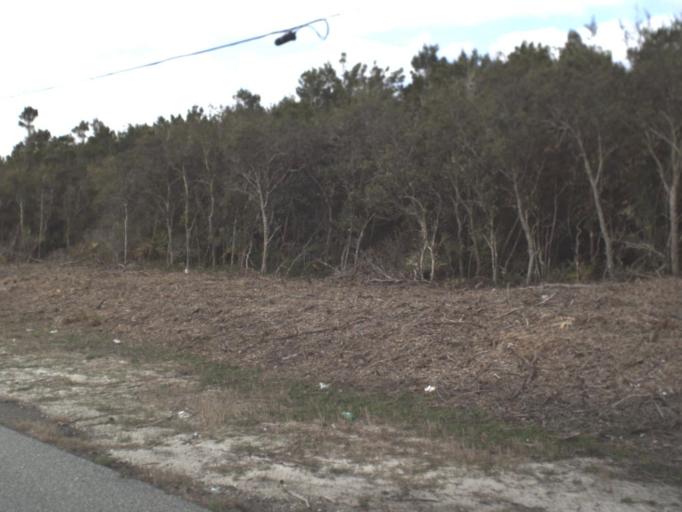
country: US
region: Florida
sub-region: Franklin County
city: Eastpoint
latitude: 29.7723
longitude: -84.7940
